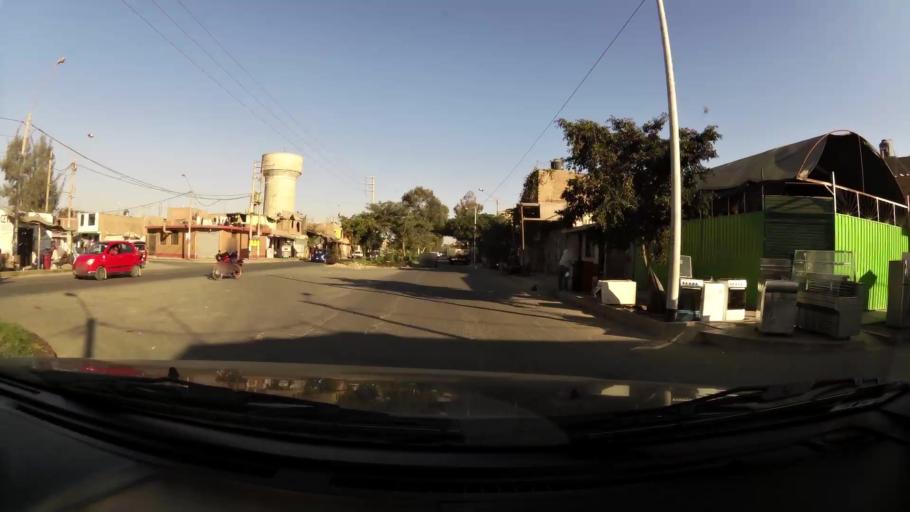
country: PE
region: Ica
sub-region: Provincia de Ica
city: Ica
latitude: -14.0624
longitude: -75.7212
